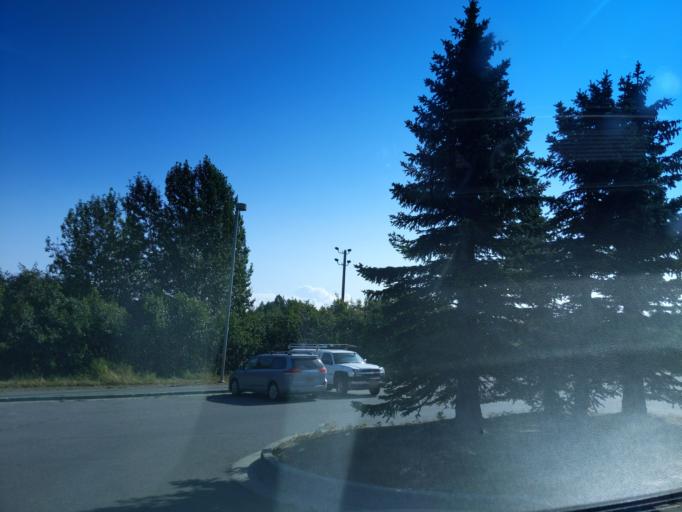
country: US
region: Alaska
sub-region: Anchorage Municipality
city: Anchorage
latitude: 61.1543
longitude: -150.0534
